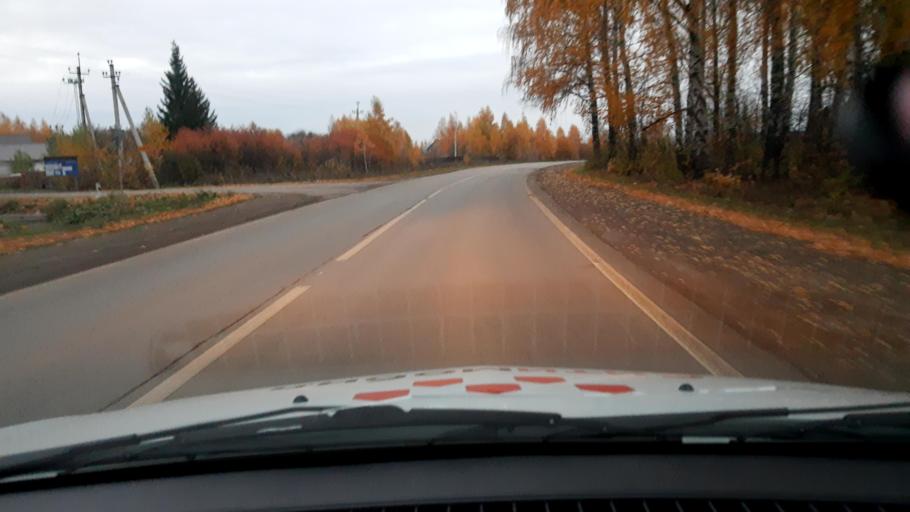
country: RU
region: Bashkortostan
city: Kabakovo
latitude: 54.7069
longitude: 56.1691
